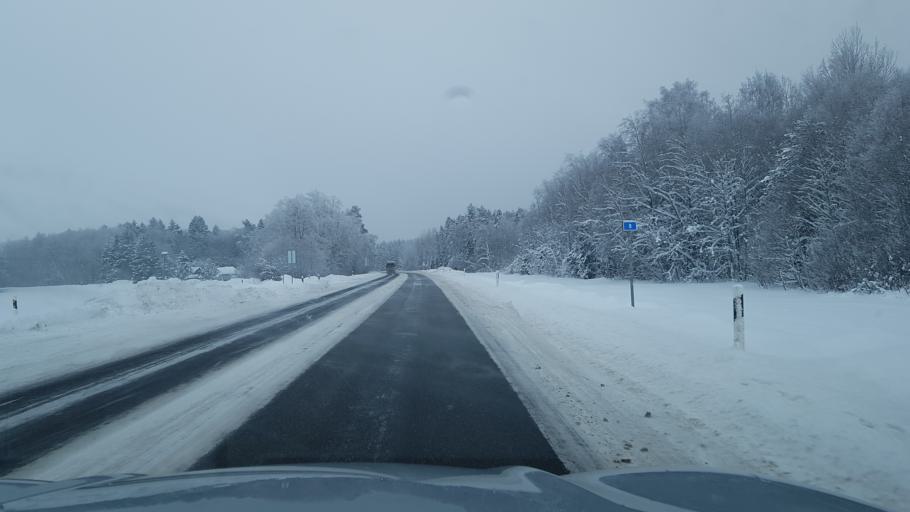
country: EE
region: Ida-Virumaa
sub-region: Johvi vald
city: Johvi
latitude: 59.3094
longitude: 27.3928
